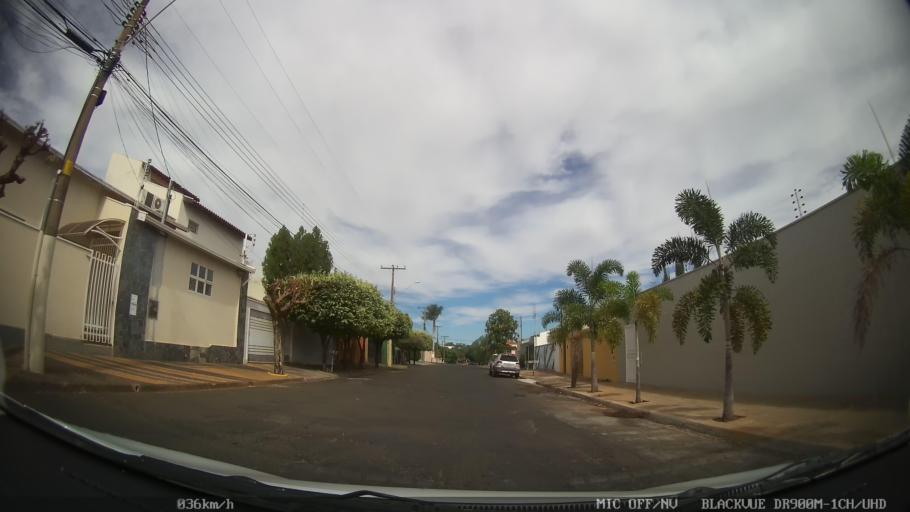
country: BR
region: Sao Paulo
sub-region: Catanduva
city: Catanduva
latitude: -21.1501
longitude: -48.9727
